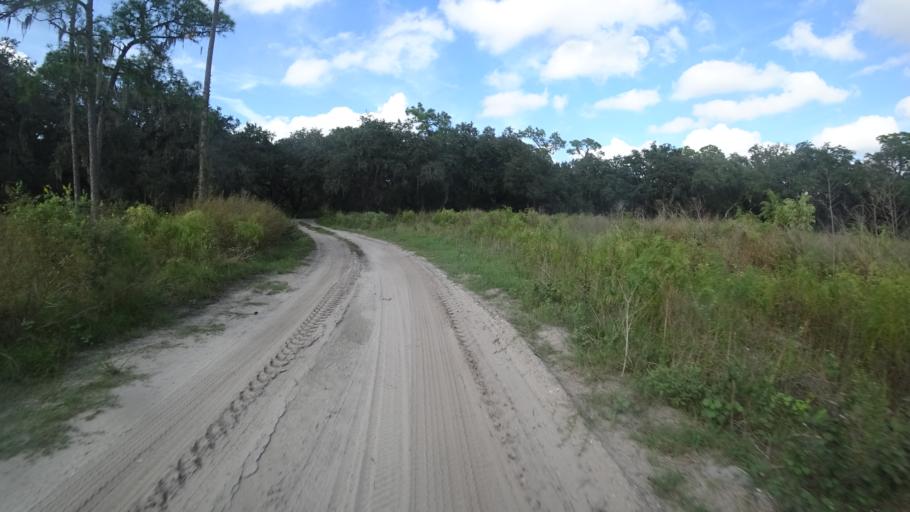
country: US
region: Florida
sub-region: DeSoto County
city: Arcadia
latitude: 27.3485
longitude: -82.1146
